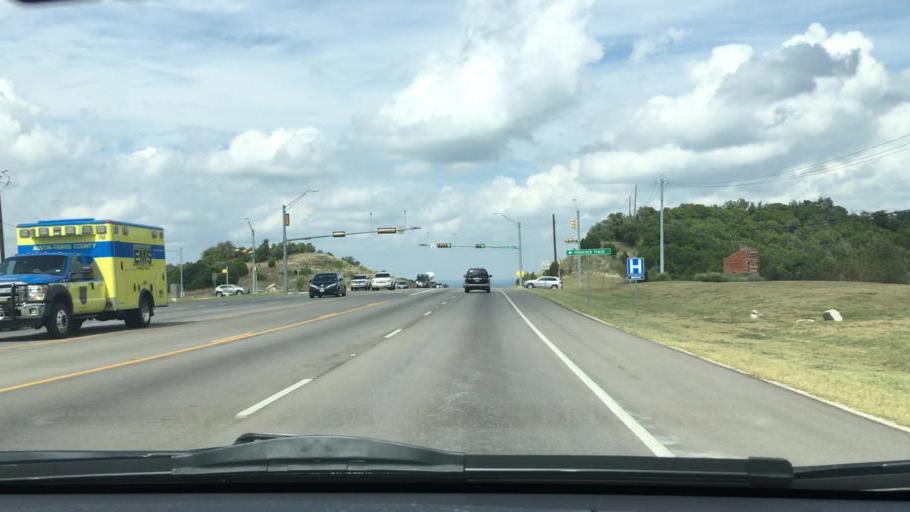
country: US
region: Texas
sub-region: Travis County
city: The Hills
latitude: 30.3337
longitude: -97.9684
